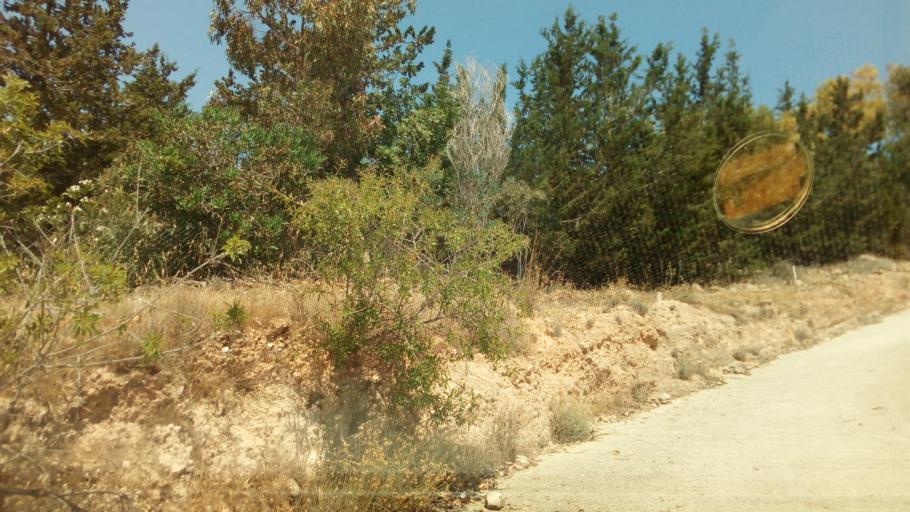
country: CY
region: Pafos
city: Mesogi
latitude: 34.7946
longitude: 32.4866
